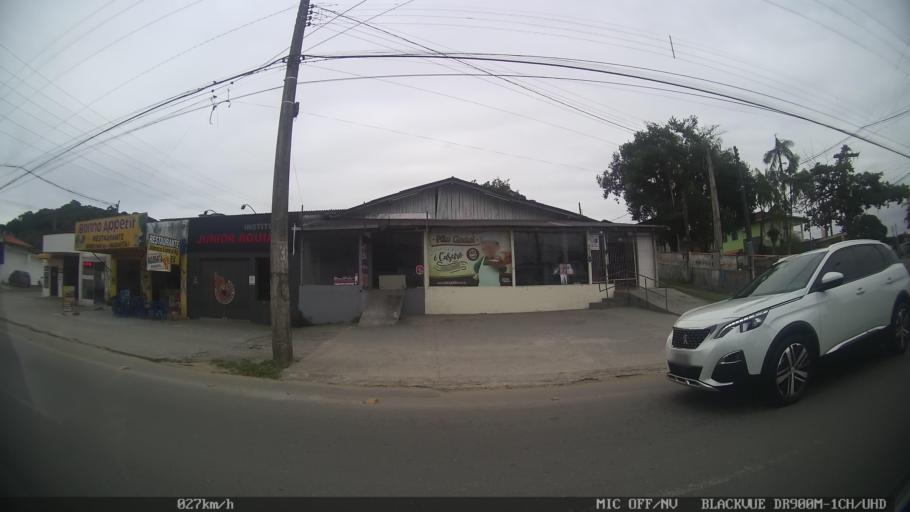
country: BR
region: Santa Catarina
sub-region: Joinville
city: Joinville
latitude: -26.2713
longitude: -48.8269
